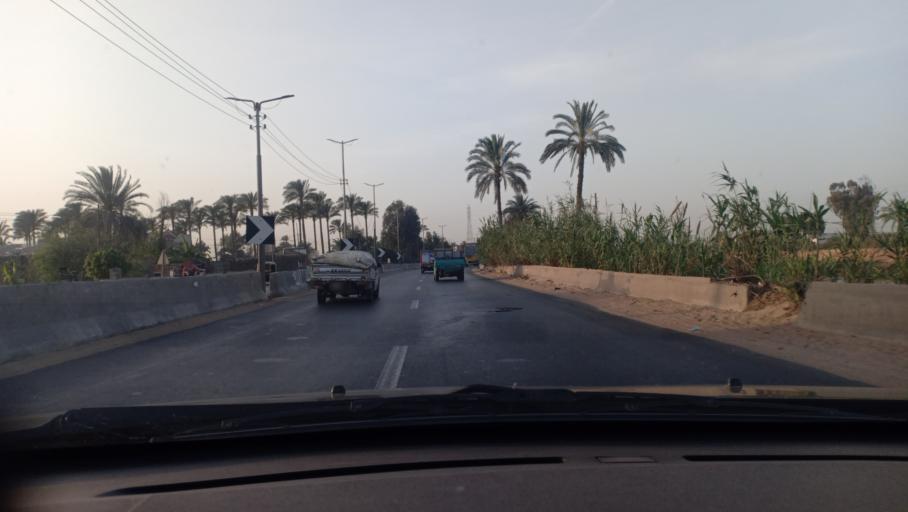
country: EG
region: Muhafazat al Minufiyah
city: Quwaysina
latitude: 30.5553
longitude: 31.2683
